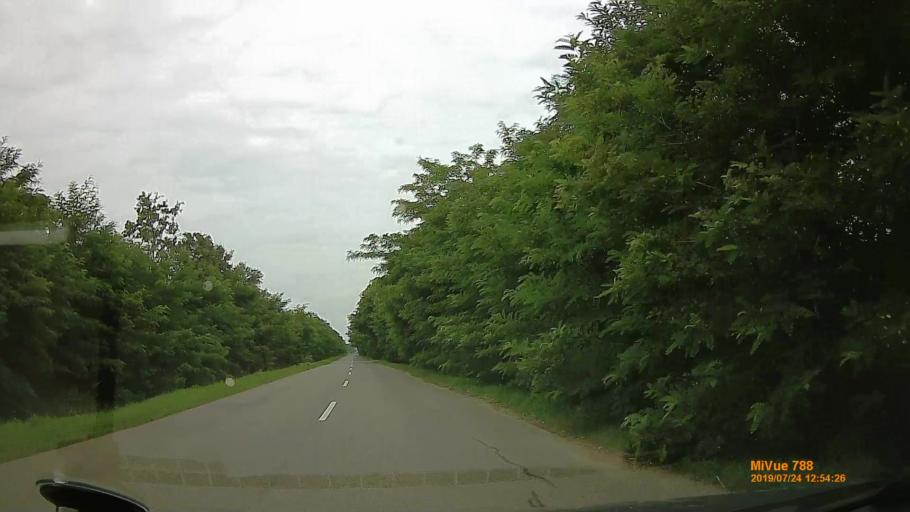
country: HU
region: Szabolcs-Szatmar-Bereg
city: Aranyosapati
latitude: 48.2155
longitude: 22.2990
